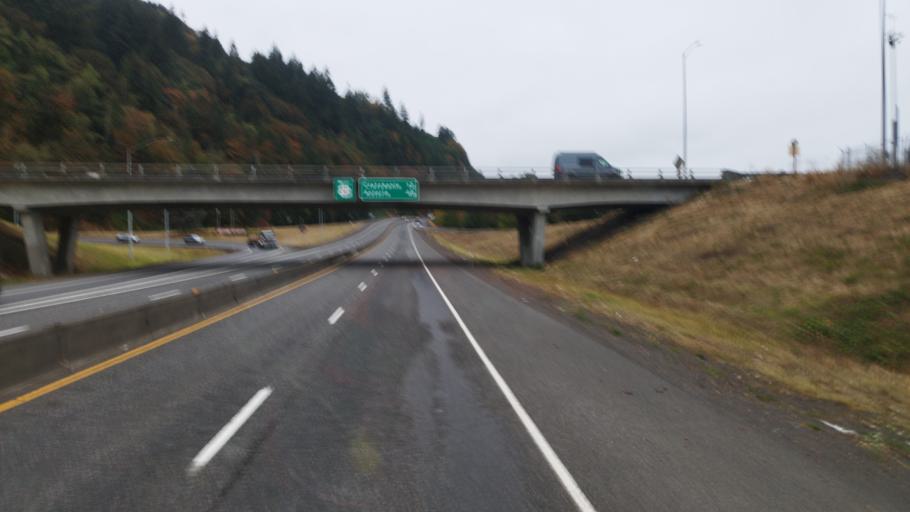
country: US
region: Oregon
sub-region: Columbia County
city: Rainier
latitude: 46.0956
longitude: -122.9686
